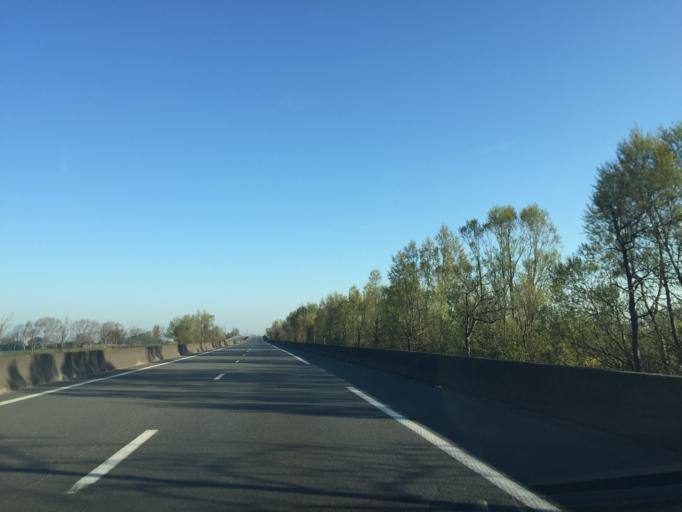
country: FR
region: Nord-Pas-de-Calais
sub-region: Departement du Nord
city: Loon-Plage
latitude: 50.9829
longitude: 2.2106
